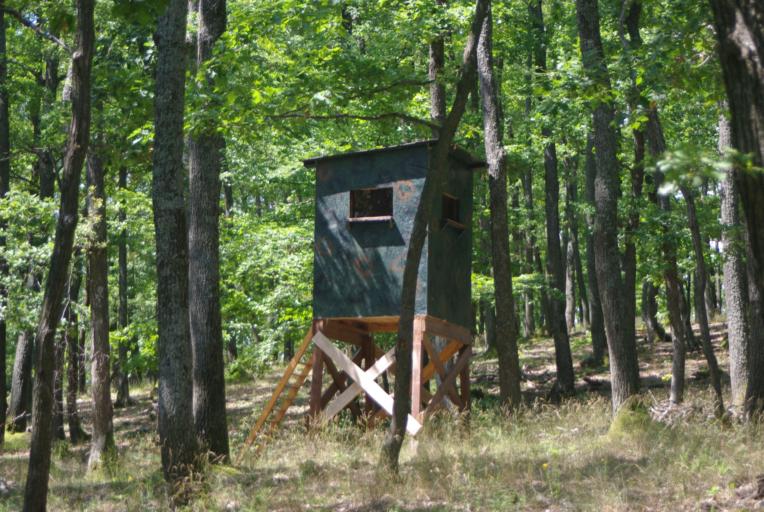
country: HU
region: Borsod-Abauj-Zemplen
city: Gonc
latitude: 48.4089
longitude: 21.3133
